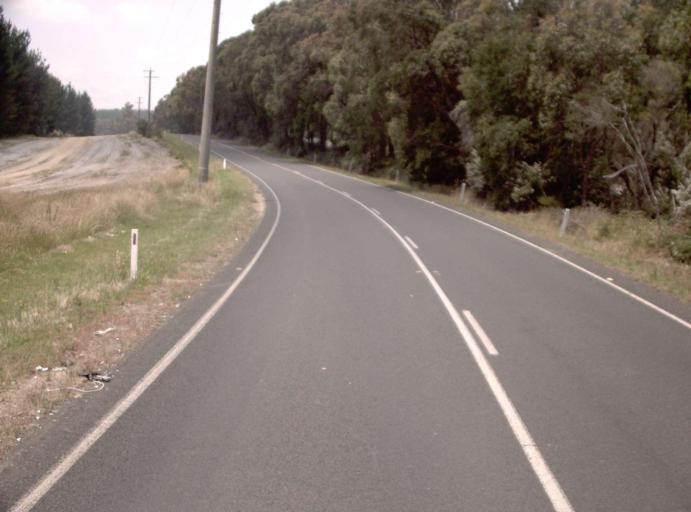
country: AU
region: Victoria
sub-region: Latrobe
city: Traralgon
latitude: -38.2608
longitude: 146.6801
